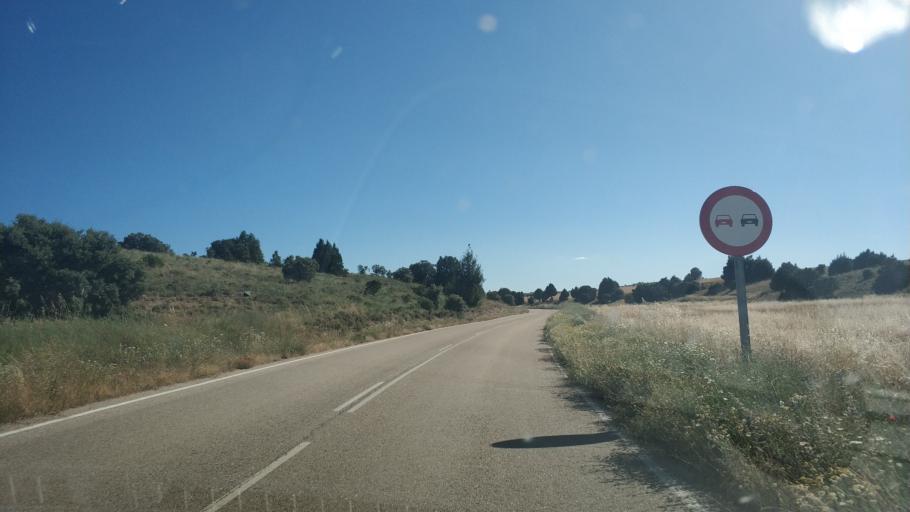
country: ES
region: Castille and Leon
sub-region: Provincia de Soria
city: San Esteban de Gormaz
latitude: 41.4911
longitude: -3.2052
